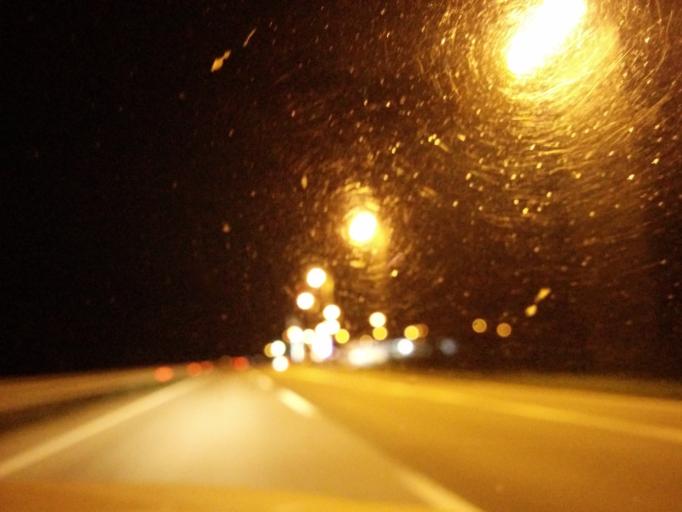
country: RS
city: Visnjicevo
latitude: 45.0404
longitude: 19.2661
